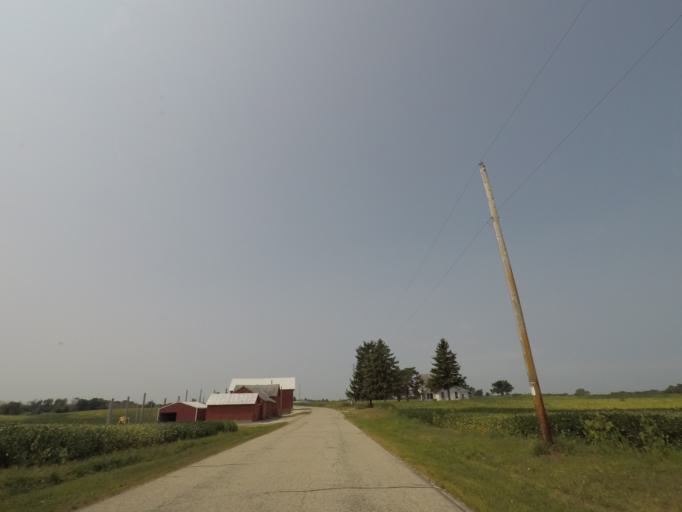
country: US
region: Wisconsin
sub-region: Waukesha County
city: Oconomowoc
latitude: 43.0662
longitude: -88.5611
